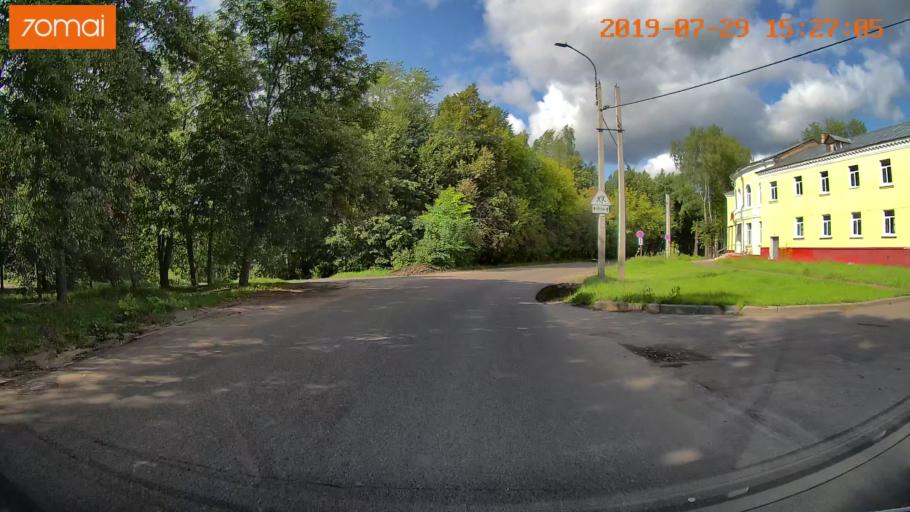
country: RU
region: Ivanovo
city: Bogorodskoye
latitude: 57.0201
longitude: 41.0055
